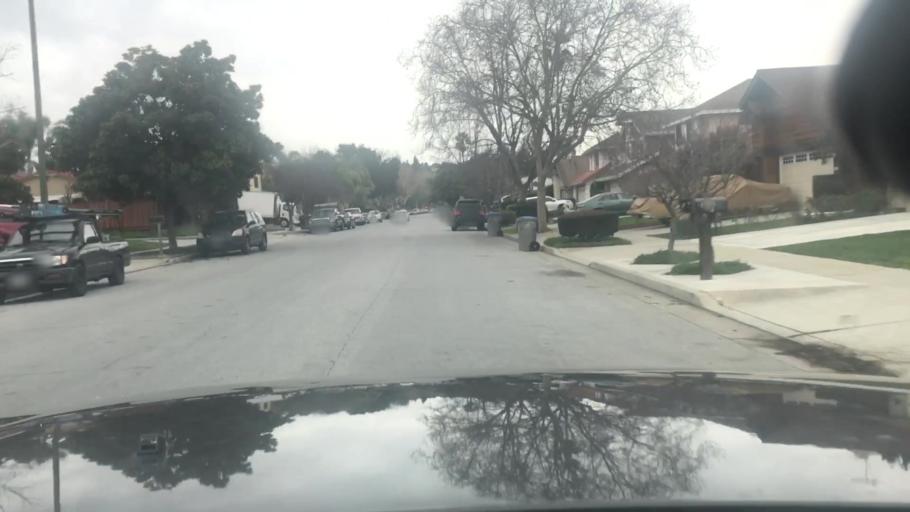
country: US
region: California
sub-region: Santa Clara County
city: Seven Trees
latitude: 37.3104
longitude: -121.8048
